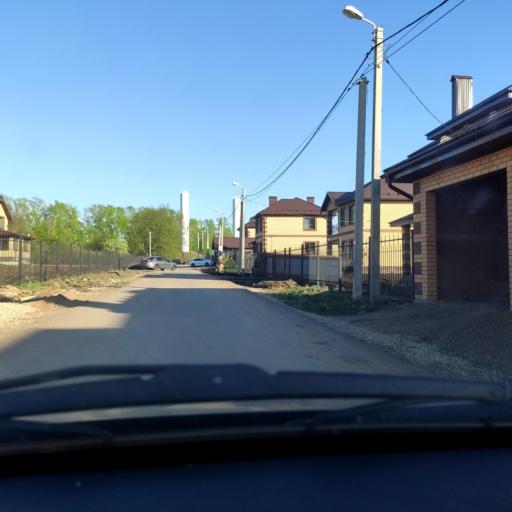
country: RU
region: Bashkortostan
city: Mikhaylovka
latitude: 54.8316
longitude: 55.8781
